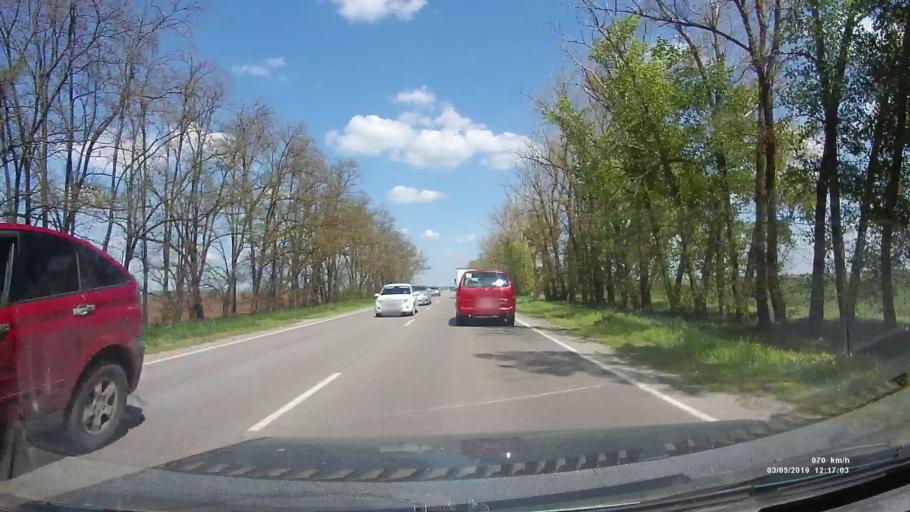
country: RU
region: Rostov
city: Melikhovskaya
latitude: 47.3788
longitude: 40.5893
